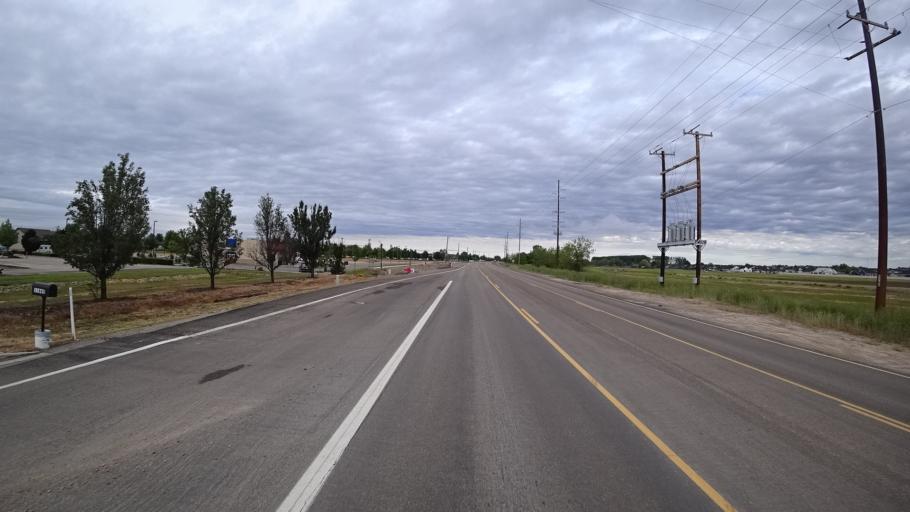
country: US
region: Idaho
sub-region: Ada County
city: Star
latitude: 43.6922
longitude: -116.4993
